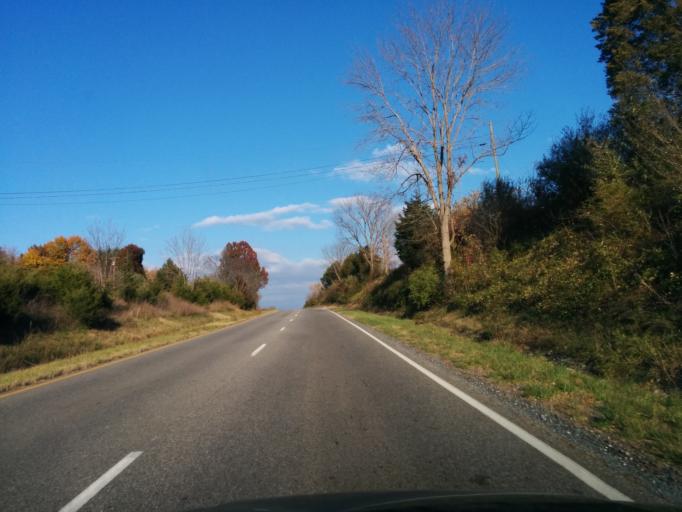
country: US
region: Virginia
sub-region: Rockbridge County
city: East Lexington
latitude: 37.8051
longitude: -79.4052
